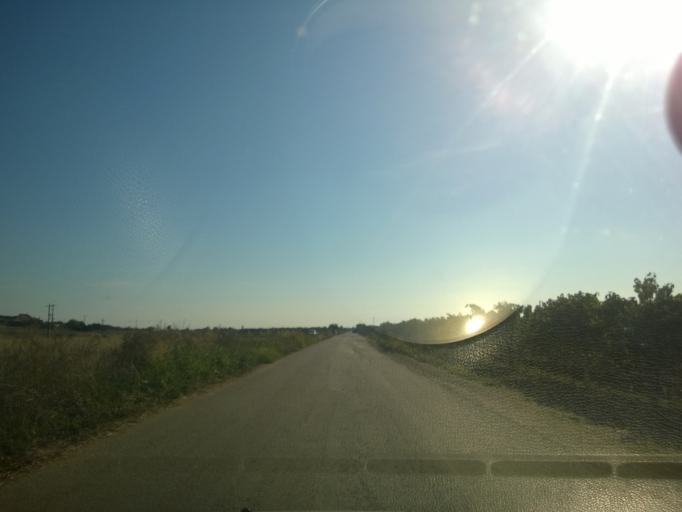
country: GR
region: Central Macedonia
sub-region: Nomos Chalkidikis
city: Nea Kallikrateia
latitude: 40.3395
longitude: 23.0465
